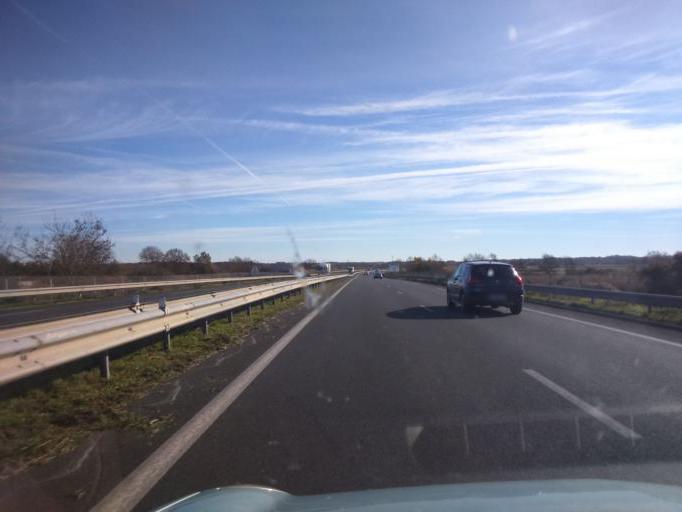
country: FR
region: Poitou-Charentes
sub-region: Departement de la Charente-Maritime
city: Saint-Laurent-de-la-Pree
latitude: 45.9804
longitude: -1.0042
